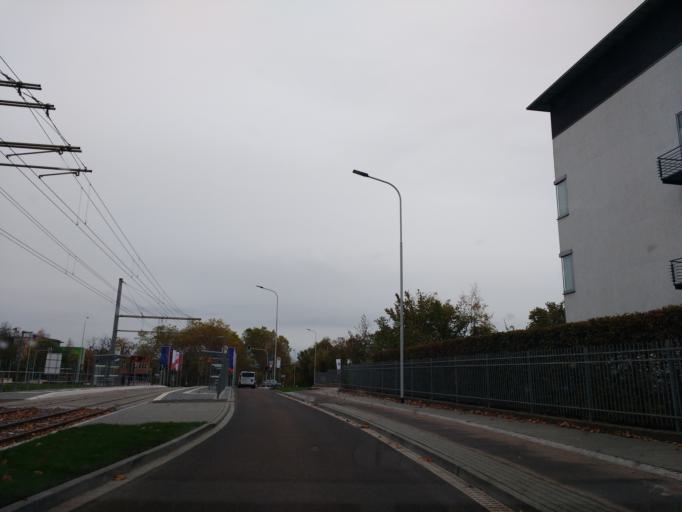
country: DE
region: Saxony-Anhalt
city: Halle Neustadt
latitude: 51.4962
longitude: 11.9384
